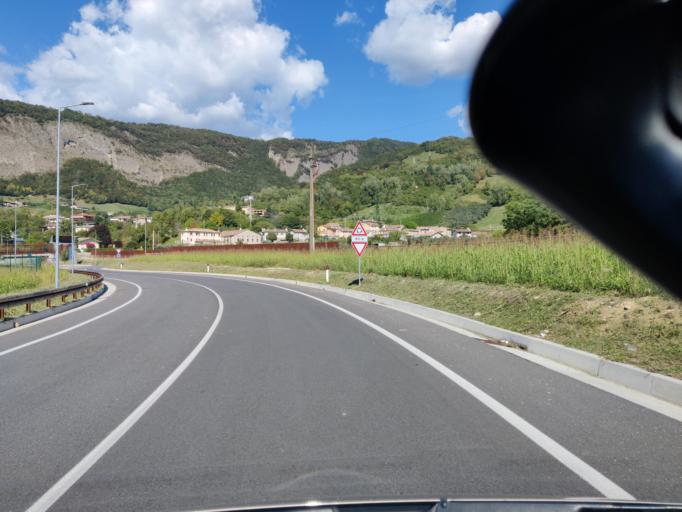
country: IT
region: Veneto
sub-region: Provincia di Treviso
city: Vittorio Veneto
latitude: 45.9955
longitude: 12.3023
